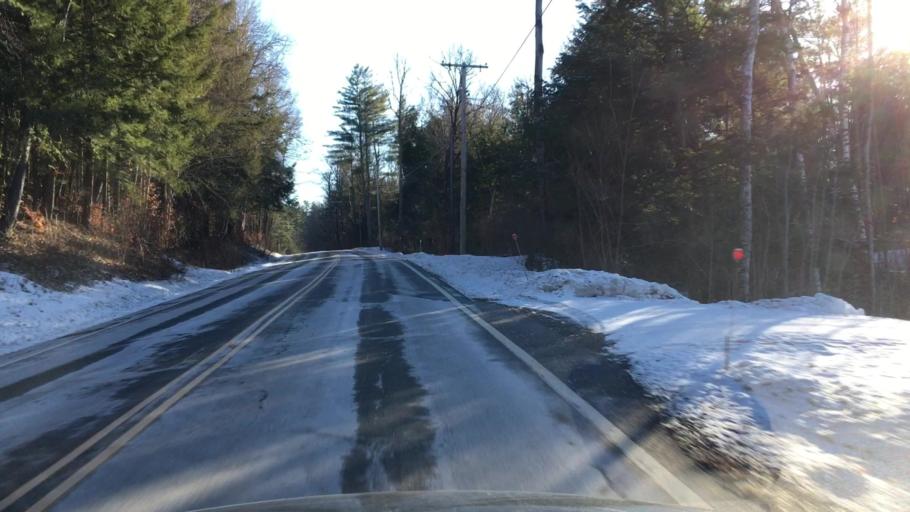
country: US
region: New Hampshire
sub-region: Grafton County
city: Woodsville
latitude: 44.2156
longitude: -72.0496
